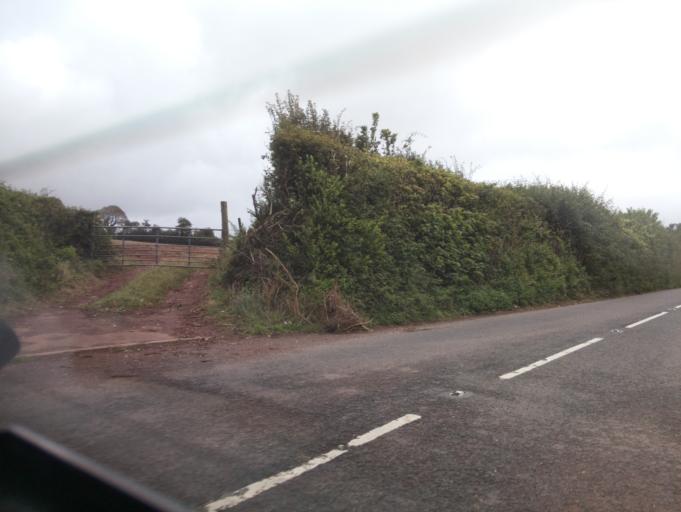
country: GB
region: England
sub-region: Devon
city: Salcombe
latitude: 50.2730
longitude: -3.6862
